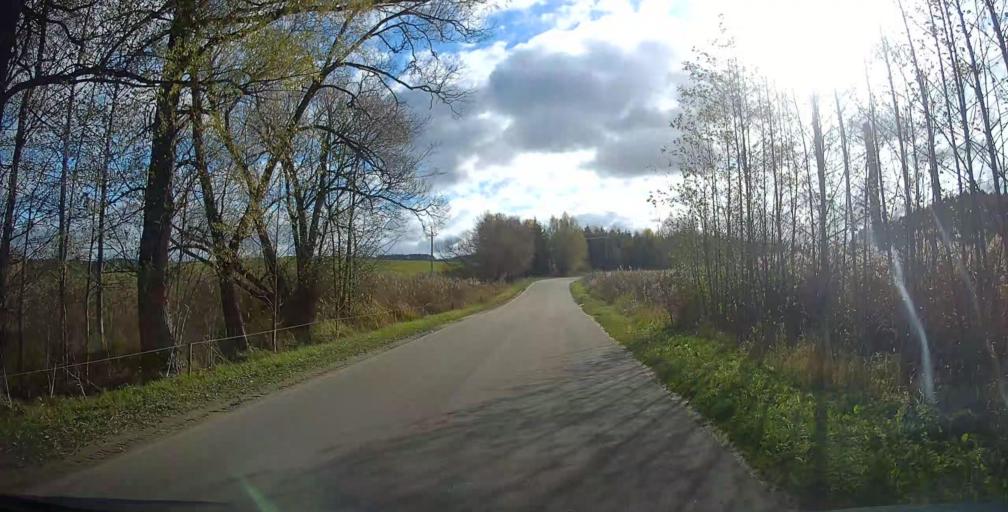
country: PL
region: Podlasie
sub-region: Suwalki
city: Suwalki
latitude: 54.2788
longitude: 22.9094
